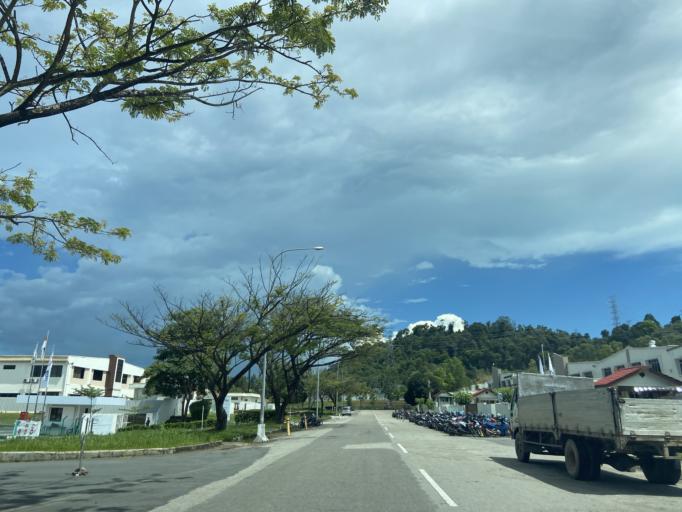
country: SG
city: Singapore
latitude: 1.0539
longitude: 104.0393
